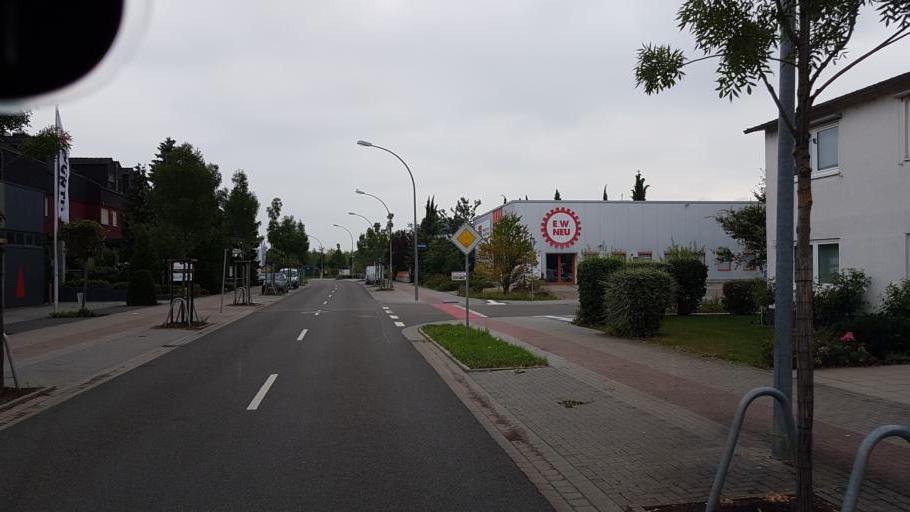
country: DE
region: Rheinland-Pfalz
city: Speyer
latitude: 49.3359
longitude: 8.4368
